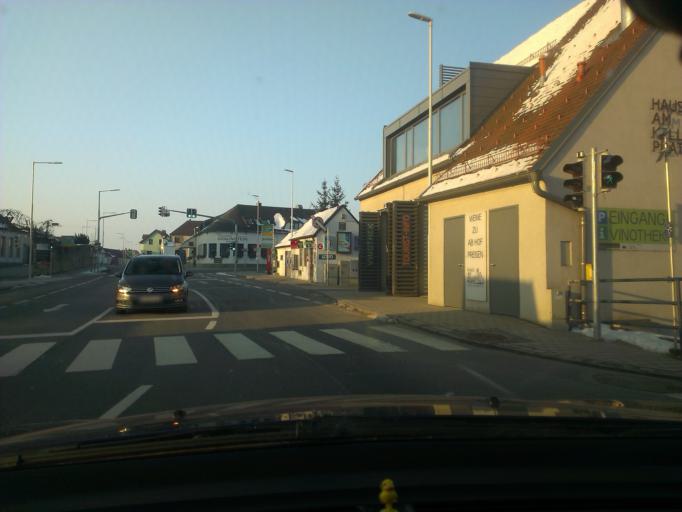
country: AT
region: Burgenland
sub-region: Eisenstadt-Umgebung
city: Breitenbrunn
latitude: 47.9149
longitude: 16.6935
